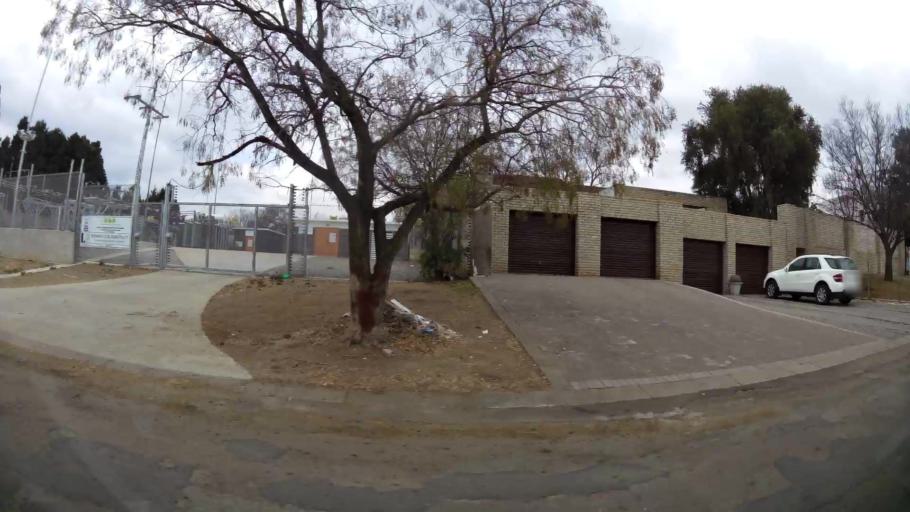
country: ZA
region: Orange Free State
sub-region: Fezile Dabi District Municipality
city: Kroonstad
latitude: -27.6857
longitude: 27.2382
